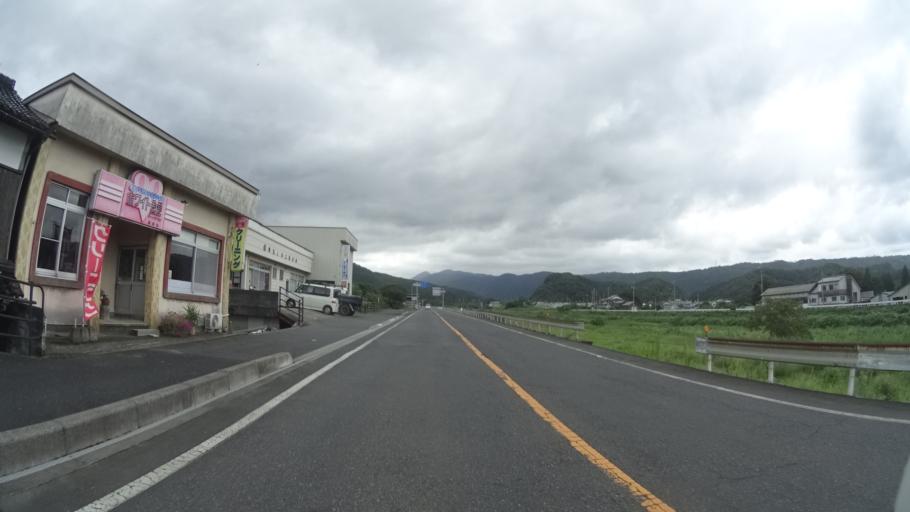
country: JP
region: Tottori
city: Tottori
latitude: 35.4630
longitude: 134.0571
